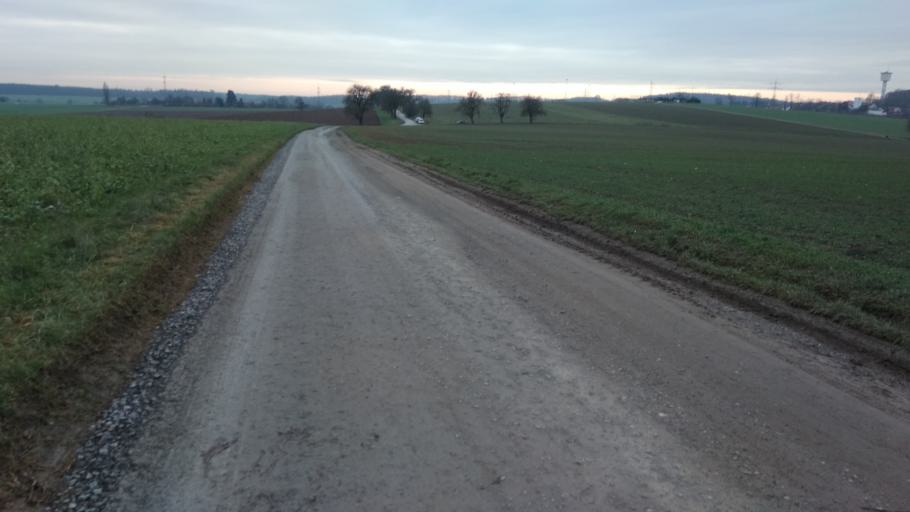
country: DE
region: Baden-Wuerttemberg
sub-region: Karlsruhe Region
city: Mosbach
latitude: 49.3540
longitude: 9.1766
